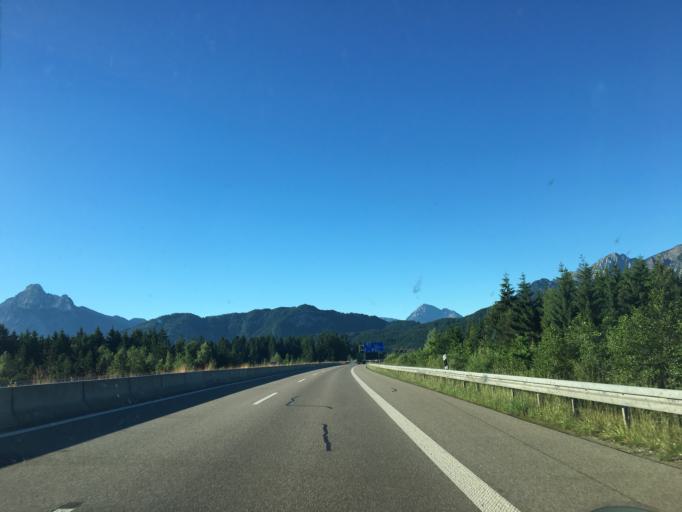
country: DE
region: Bavaria
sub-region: Swabia
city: Hopferau
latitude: 47.5867
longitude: 10.6597
